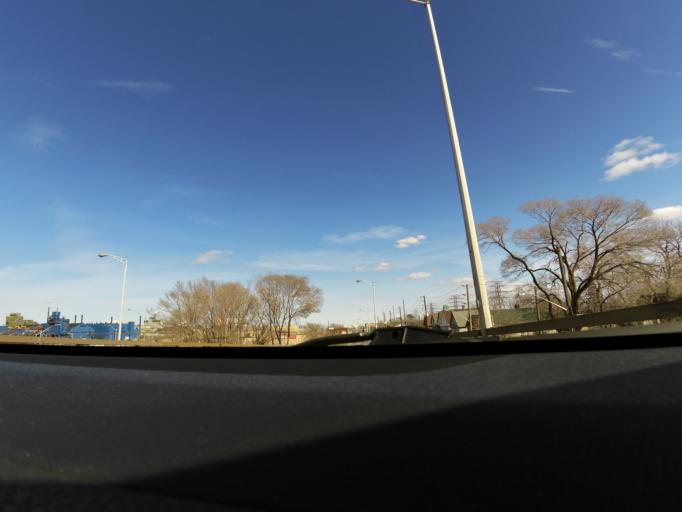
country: CA
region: Ontario
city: Hamilton
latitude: 43.2638
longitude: -79.8257
